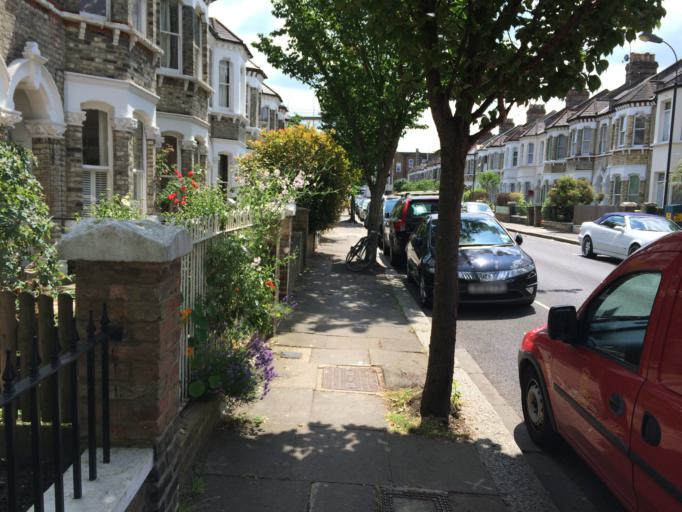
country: GB
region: England
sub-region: Greater London
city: Hammersmith
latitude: 51.5078
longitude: -0.2317
